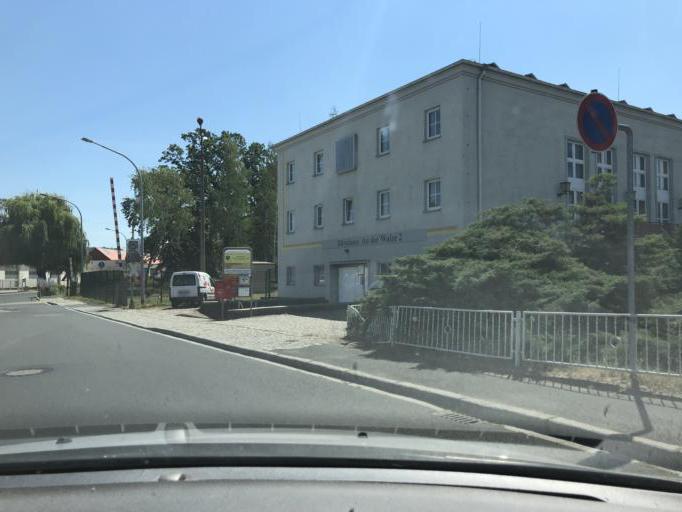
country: DE
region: Saxony
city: Coswig
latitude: 51.1196
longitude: 13.5850
